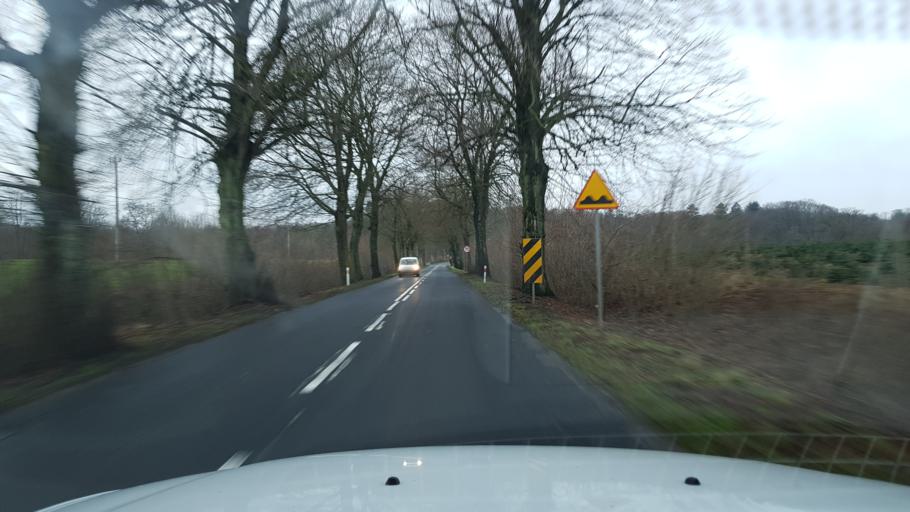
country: PL
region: West Pomeranian Voivodeship
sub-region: Powiat gryficki
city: Brojce
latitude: 54.0566
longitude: 15.3675
